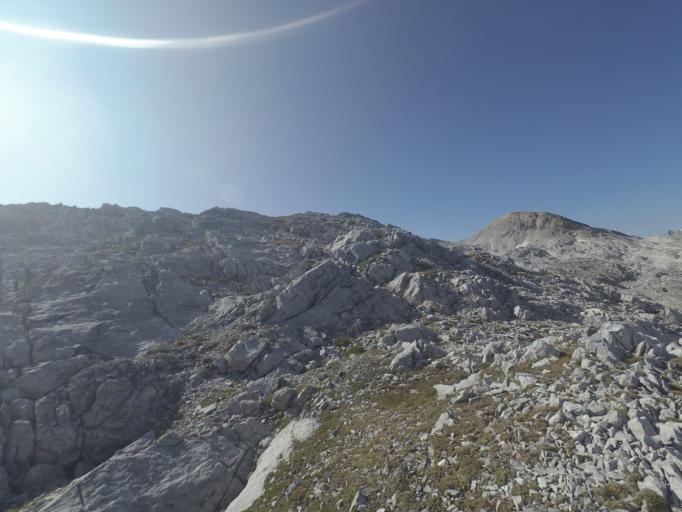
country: AT
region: Salzburg
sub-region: Politischer Bezirk Sankt Johann im Pongau
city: Kleinarl
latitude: 47.2142
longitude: 13.4010
